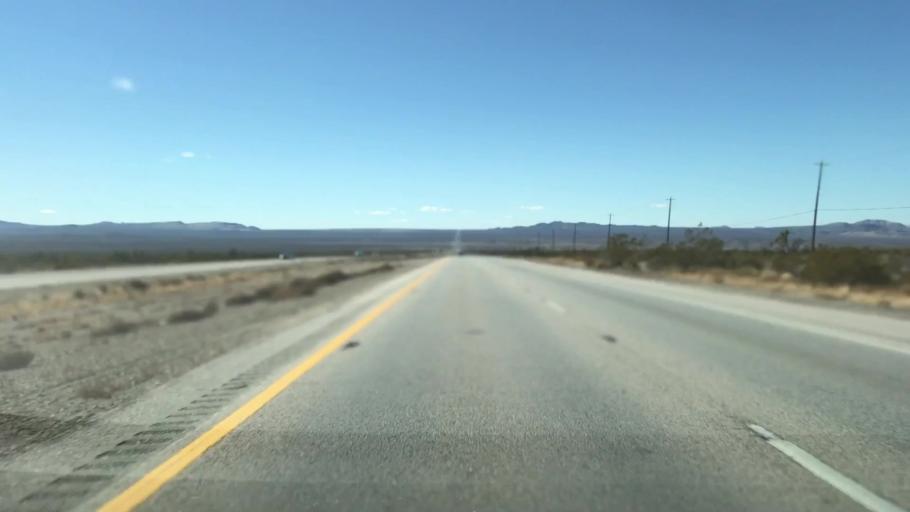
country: US
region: Nevada
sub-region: Clark County
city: Sandy Valley
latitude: 35.4655
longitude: -115.6140
